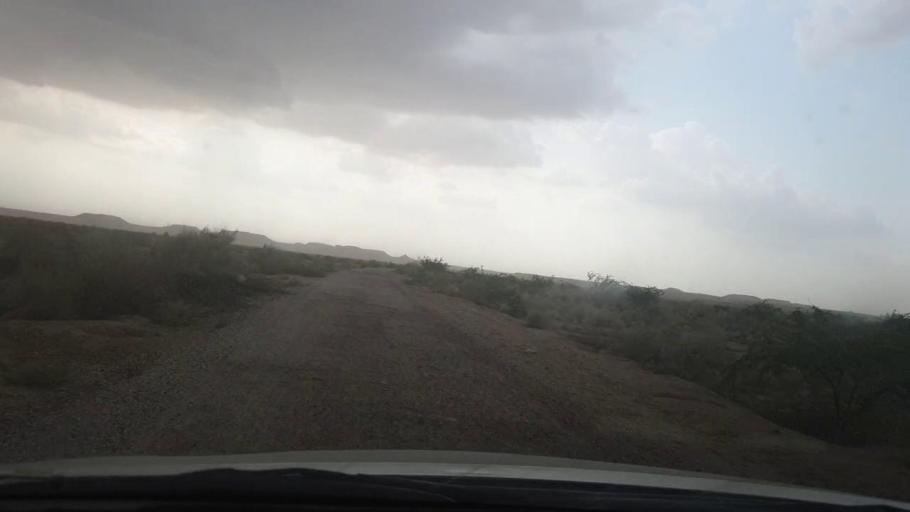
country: PK
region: Sindh
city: Khairpur
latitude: 27.4406
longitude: 68.9782
